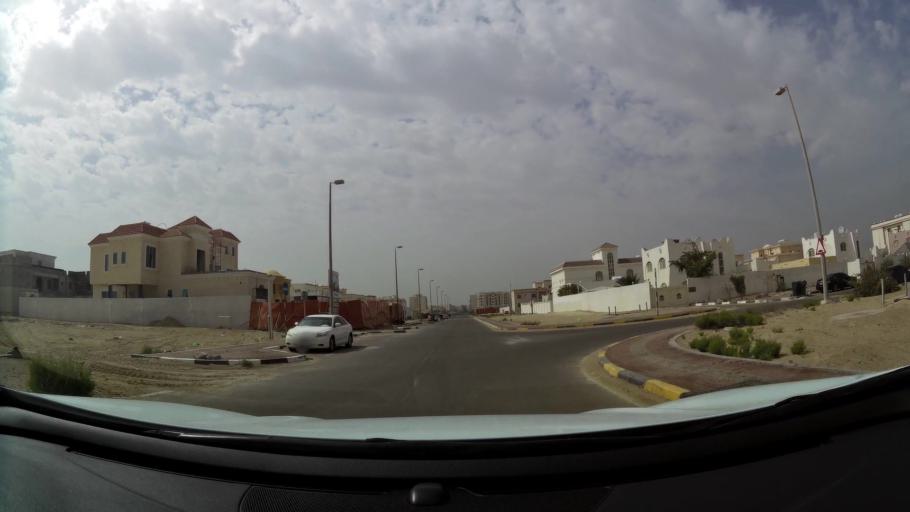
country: AE
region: Abu Dhabi
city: Abu Dhabi
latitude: 24.3180
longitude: 54.6258
